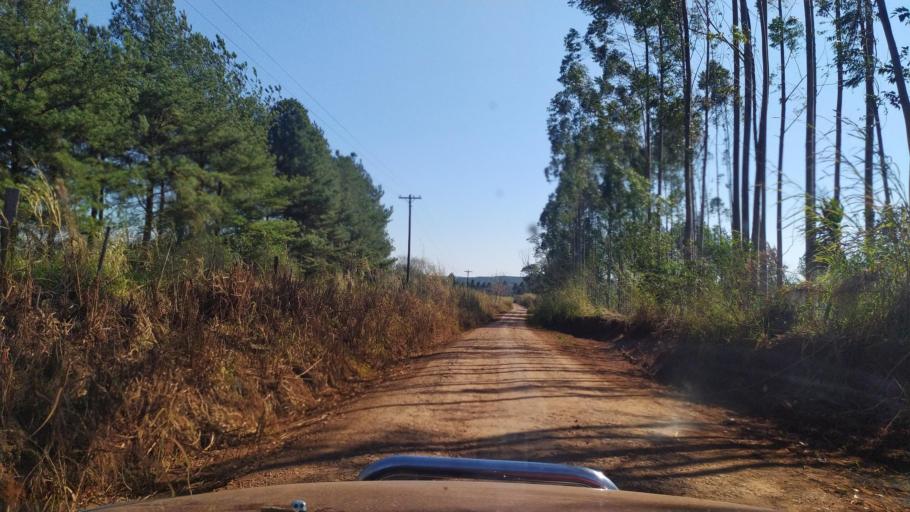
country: AR
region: Misiones
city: El Alcazar
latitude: -26.7162
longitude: -54.6973
